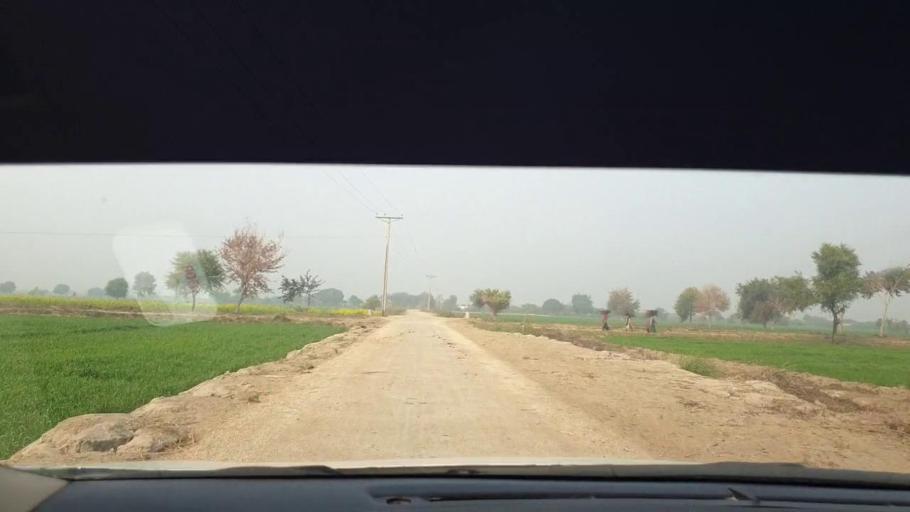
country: PK
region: Sindh
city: Berani
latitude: 25.7981
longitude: 68.8519
